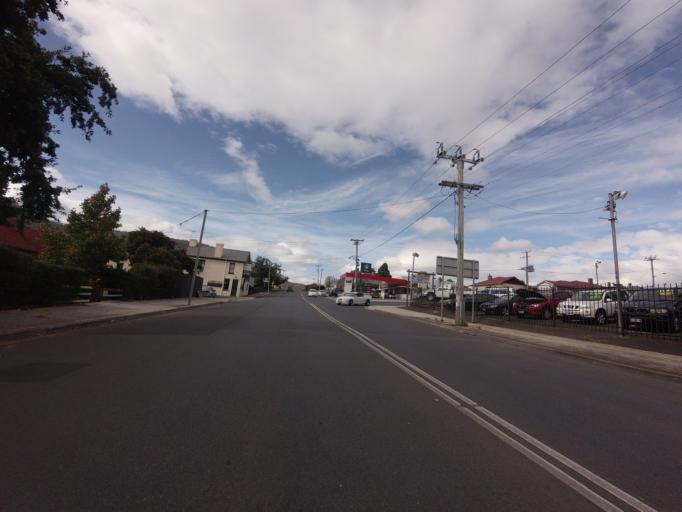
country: AU
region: Tasmania
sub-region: Derwent Valley
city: New Norfolk
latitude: -42.7792
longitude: 147.0605
